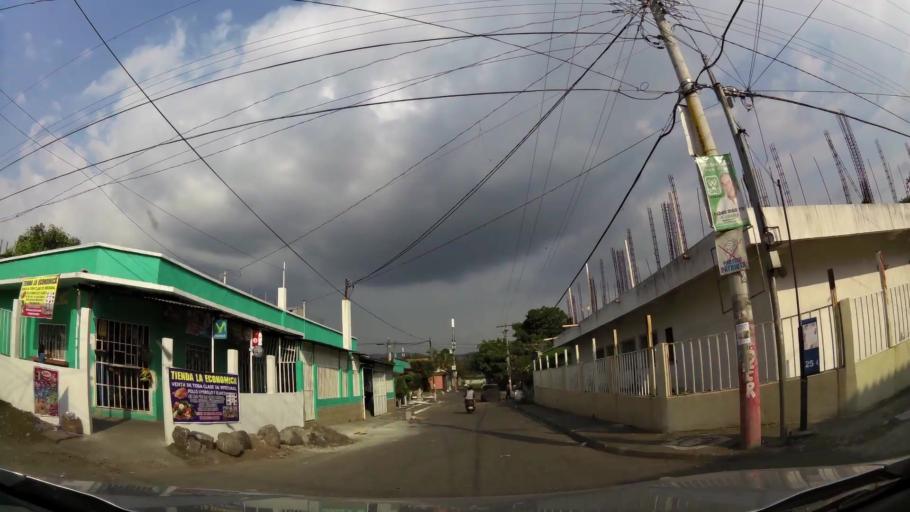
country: GT
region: Escuintla
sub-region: Municipio de Escuintla
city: Escuintla
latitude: 14.3145
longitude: -90.7950
